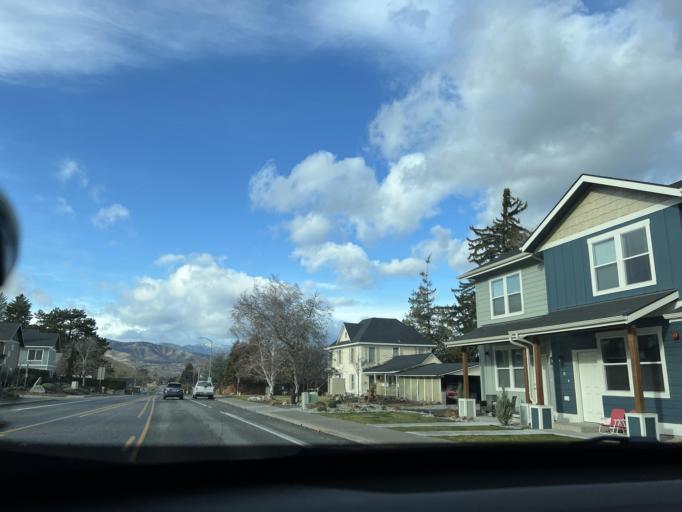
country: US
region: Washington
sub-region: Chelan County
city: Chelan
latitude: 47.8359
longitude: -120.0217
